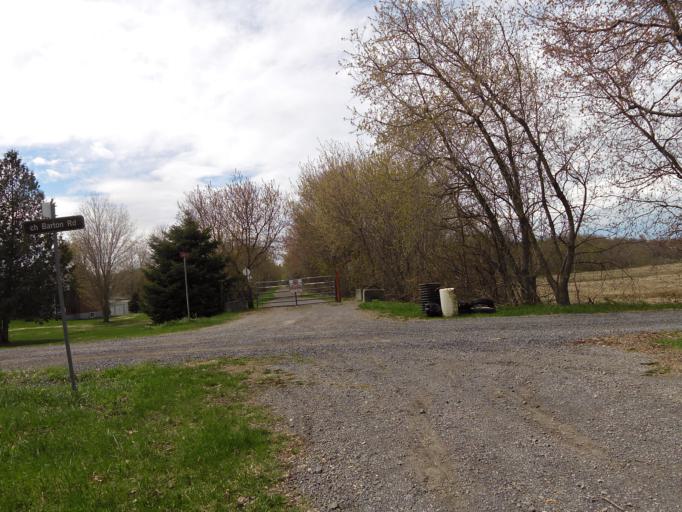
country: CA
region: Ontario
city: Hawkesbury
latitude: 45.5322
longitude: -74.6823
